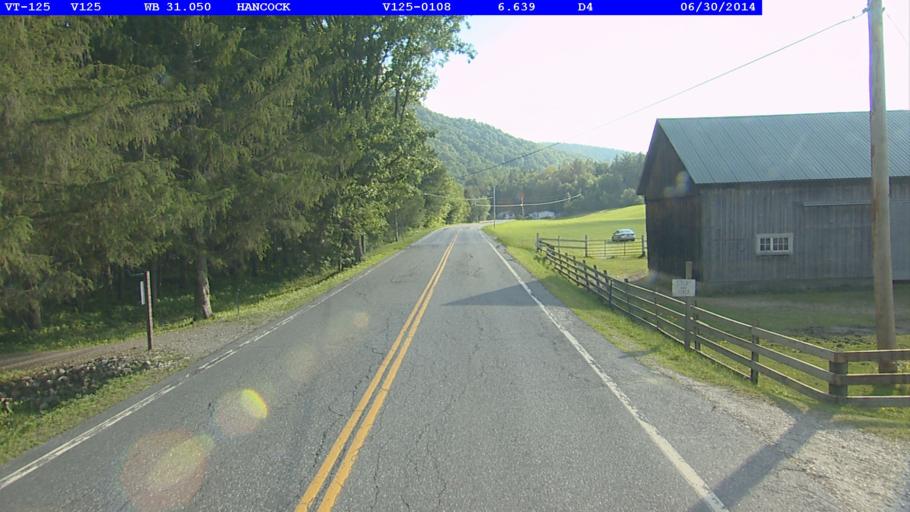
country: US
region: Vermont
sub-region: Orange County
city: Randolph
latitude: 43.9274
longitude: -72.8526
